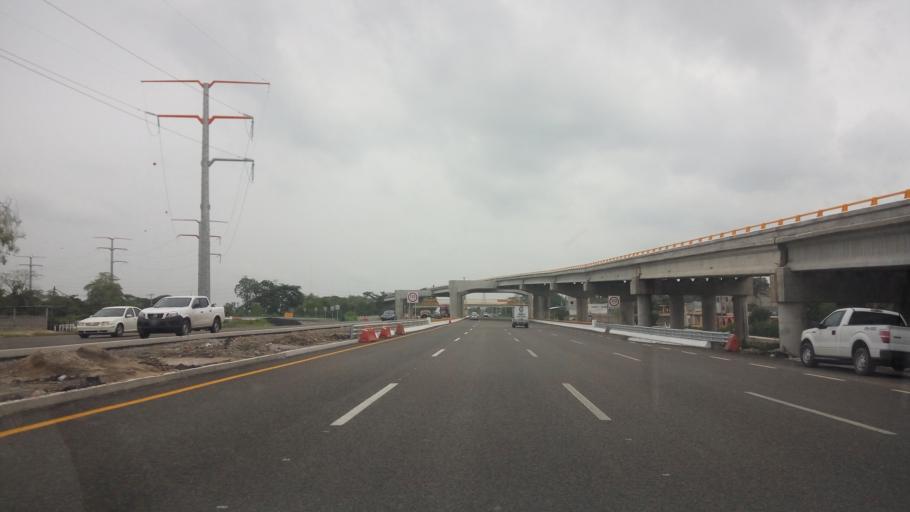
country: MX
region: Tabasco
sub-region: Centro
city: Anacleto Canabal 2da. Seccion
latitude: 17.9802
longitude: -93.0378
